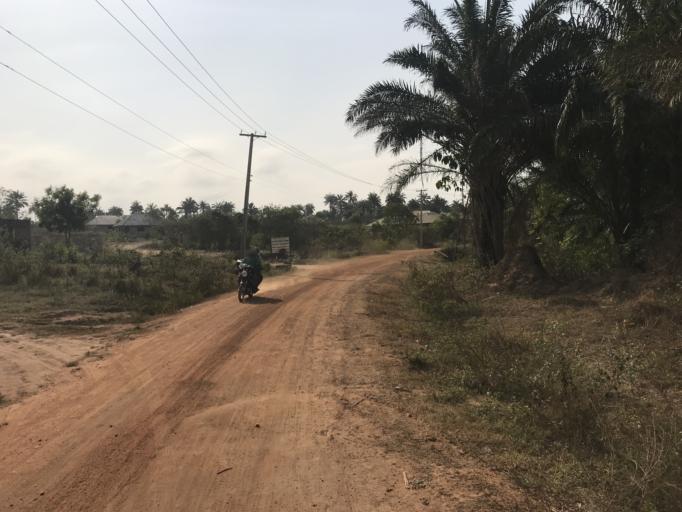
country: NG
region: Osun
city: Iwo
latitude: 7.6162
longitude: 4.1463
